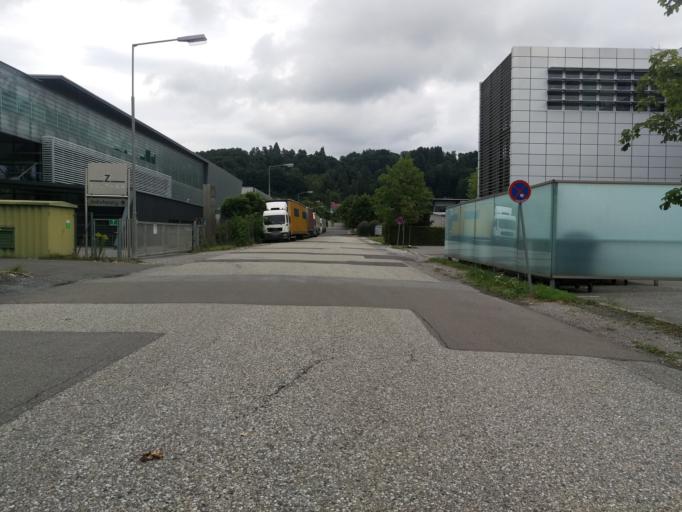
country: AT
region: Styria
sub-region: Politischer Bezirk Graz-Umgebung
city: Raaba
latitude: 47.0447
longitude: 15.4792
